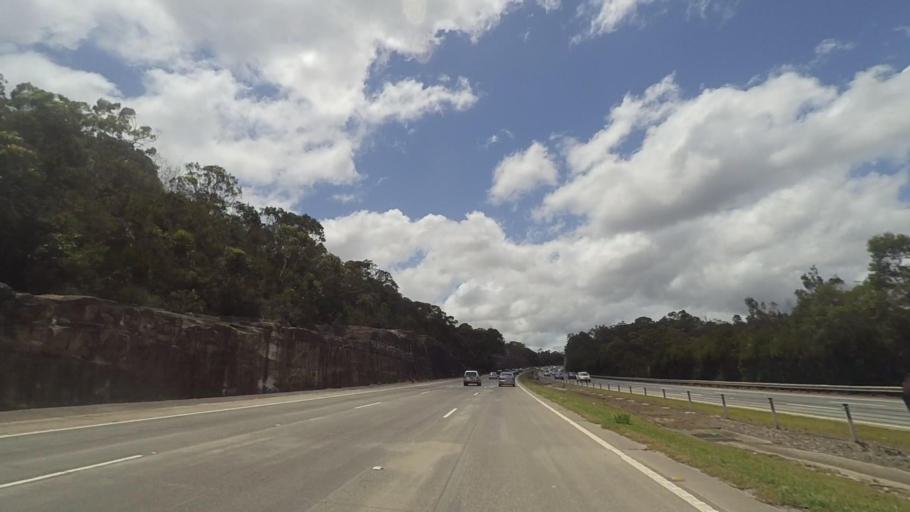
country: AU
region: New South Wales
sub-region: Hornsby Shire
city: Mount Colah
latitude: -33.6685
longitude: 151.1215
